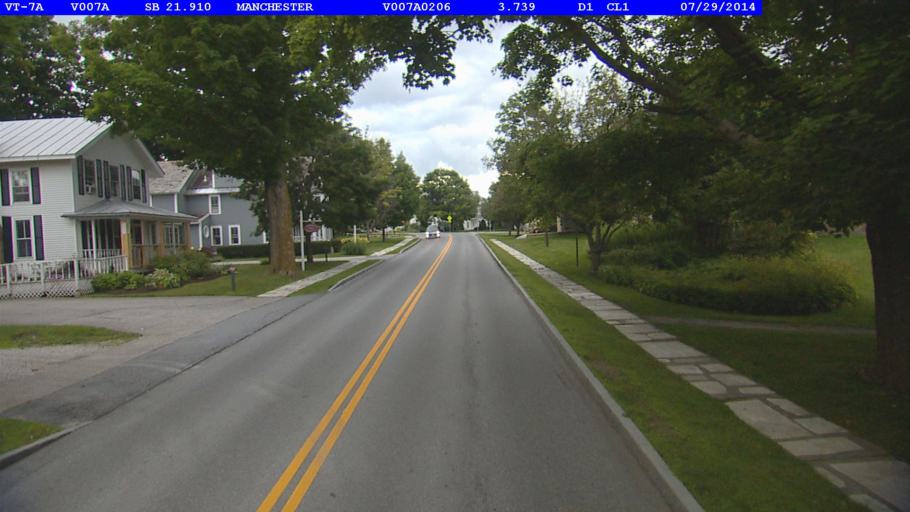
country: US
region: Vermont
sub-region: Bennington County
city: Manchester Center
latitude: 43.1643
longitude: -73.0713
